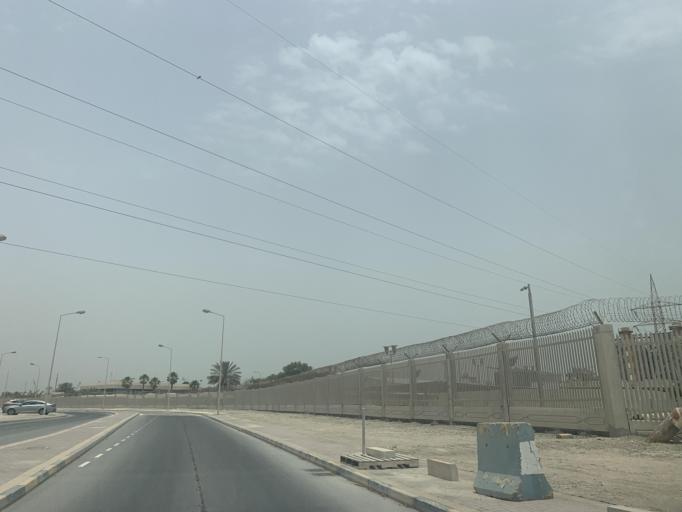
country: BH
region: Northern
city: Sitrah
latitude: 26.1808
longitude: 50.6233
